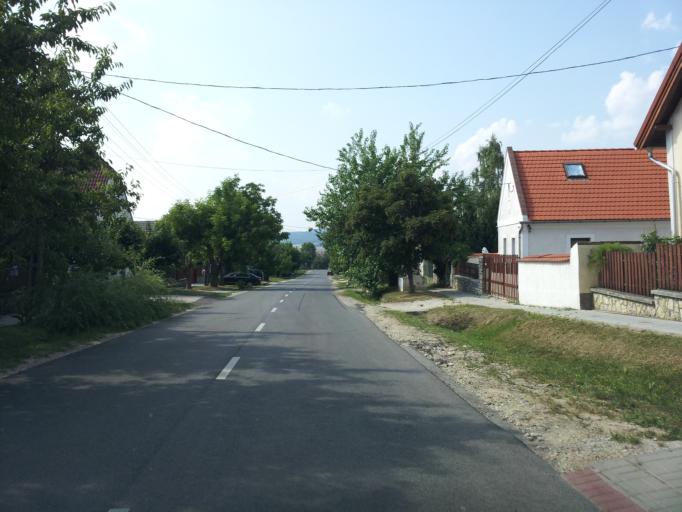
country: HU
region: Veszprem
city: Balatonfured
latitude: 47.0047
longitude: 17.7904
